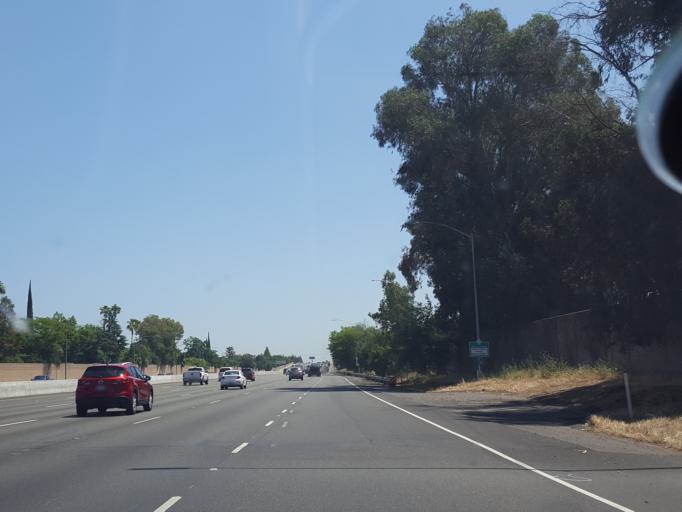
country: US
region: California
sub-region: Sacramento County
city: Rosemont
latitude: 38.5593
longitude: -121.3725
